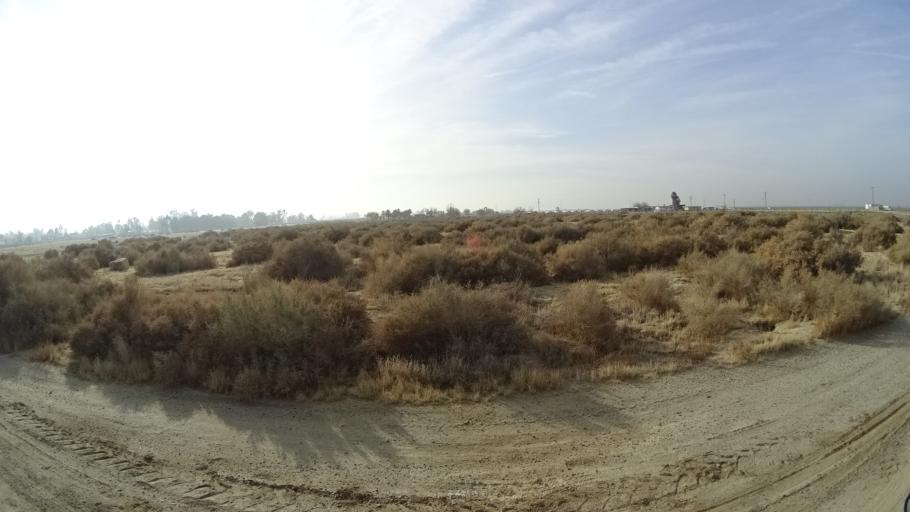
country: US
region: California
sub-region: Kern County
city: Lamont
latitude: 35.3251
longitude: -118.9462
